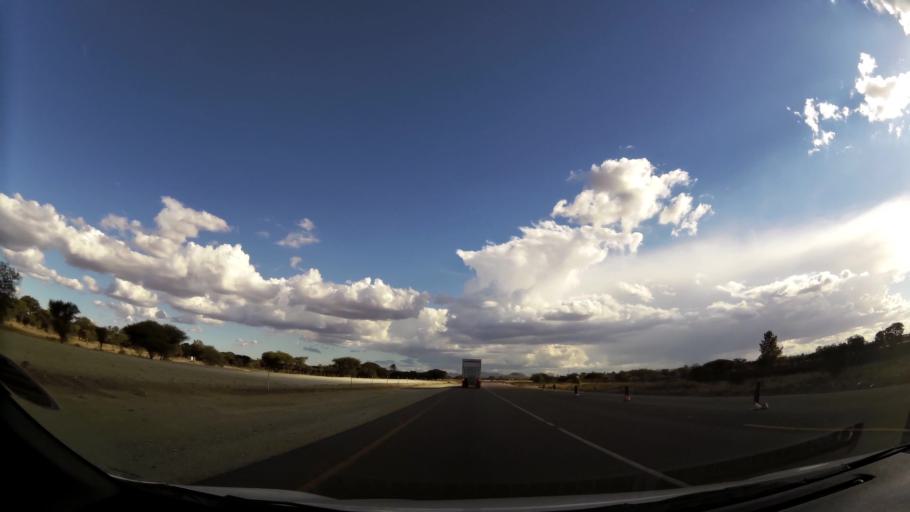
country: ZA
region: Limpopo
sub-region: Capricorn District Municipality
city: Polokwane
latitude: -23.9337
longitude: 29.4659
